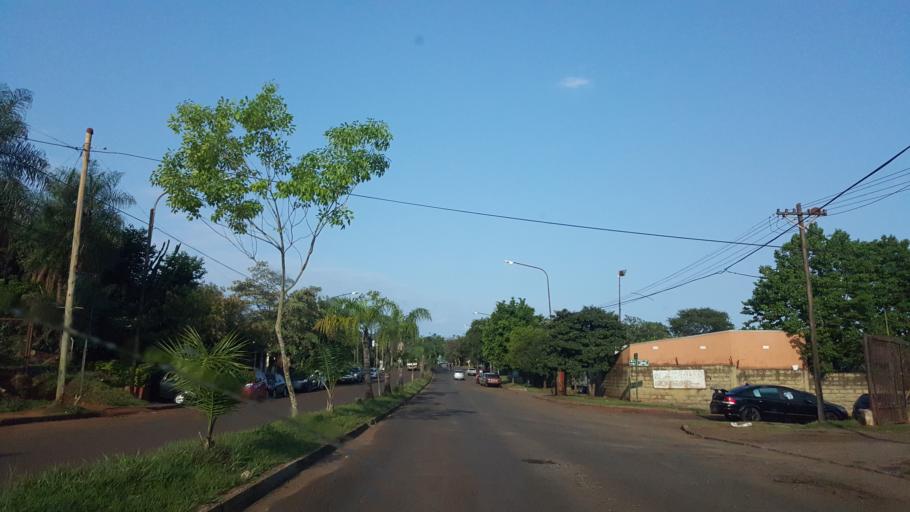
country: AR
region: Misiones
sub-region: Departamento de Capital
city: Posadas
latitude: -27.4012
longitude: -55.9016
